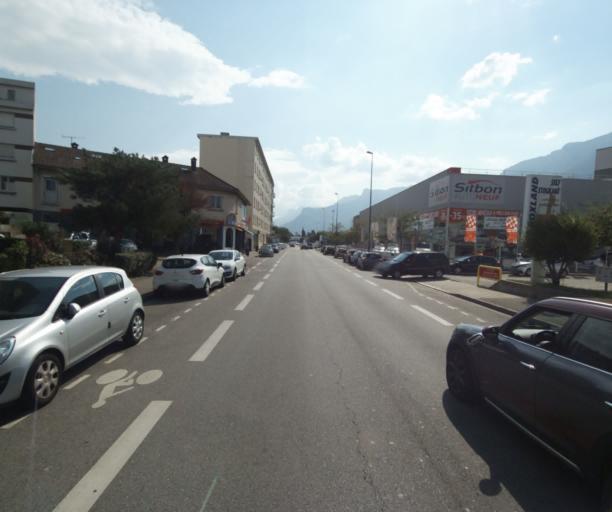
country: FR
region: Rhone-Alpes
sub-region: Departement de l'Isere
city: Grenoble
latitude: 45.1631
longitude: 5.7169
